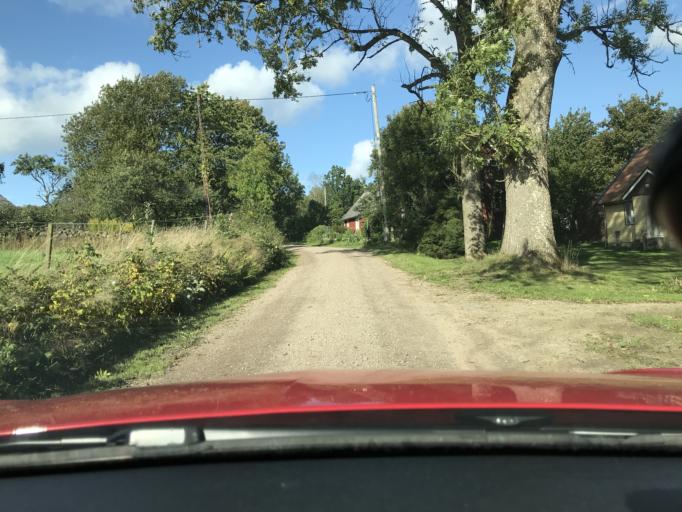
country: SE
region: Skane
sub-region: Hassleholms Kommun
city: Sosdala
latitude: 56.0006
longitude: 13.7045
